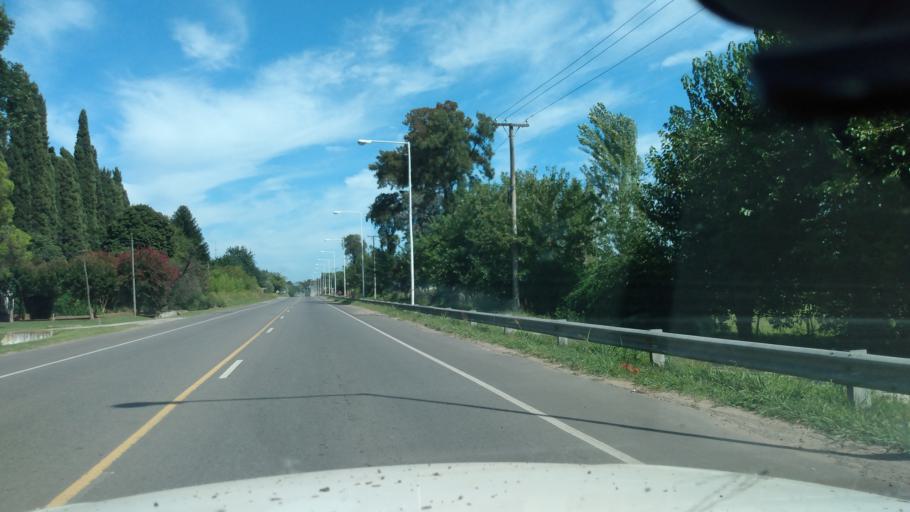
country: AR
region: Buenos Aires
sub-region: Partido de Lujan
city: Lujan
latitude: -34.5504
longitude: -59.1295
